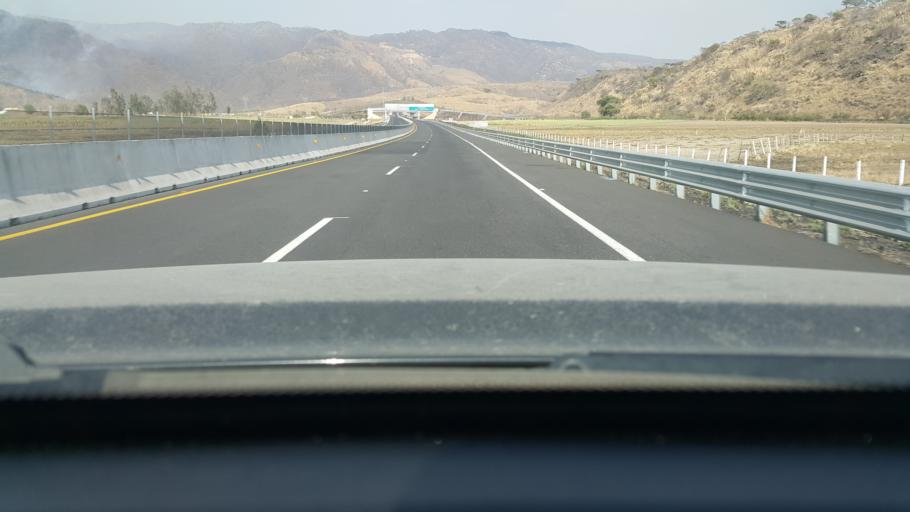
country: MX
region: Nayarit
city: Jala
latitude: 21.0773
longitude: -104.4384
